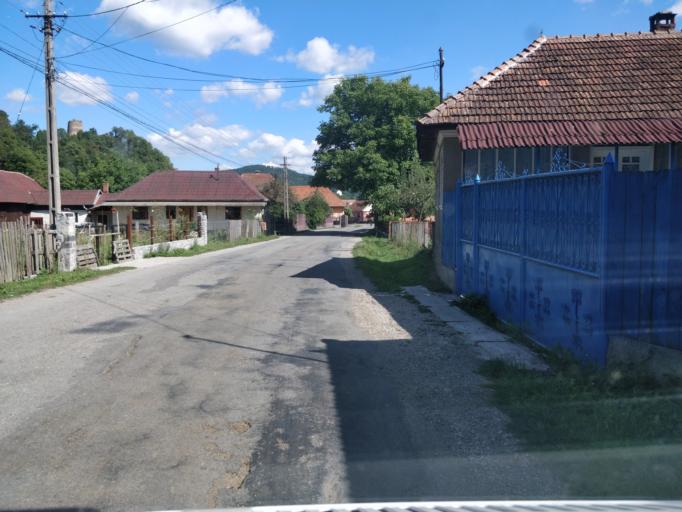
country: RO
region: Cluj
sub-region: Comuna Poeni
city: Poeni
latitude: 46.8764
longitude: 22.8795
